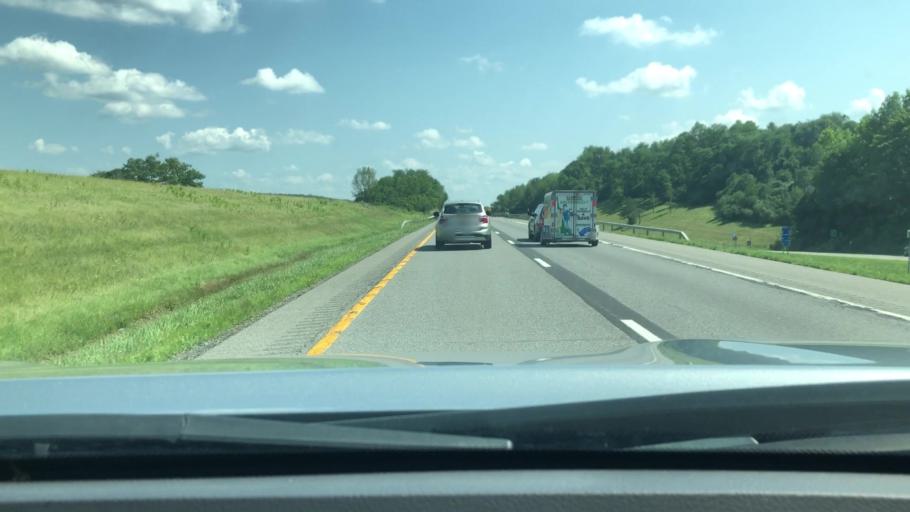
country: US
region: New York
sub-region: Putnam County
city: Lake Carmel
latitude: 41.4756
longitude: -73.6502
